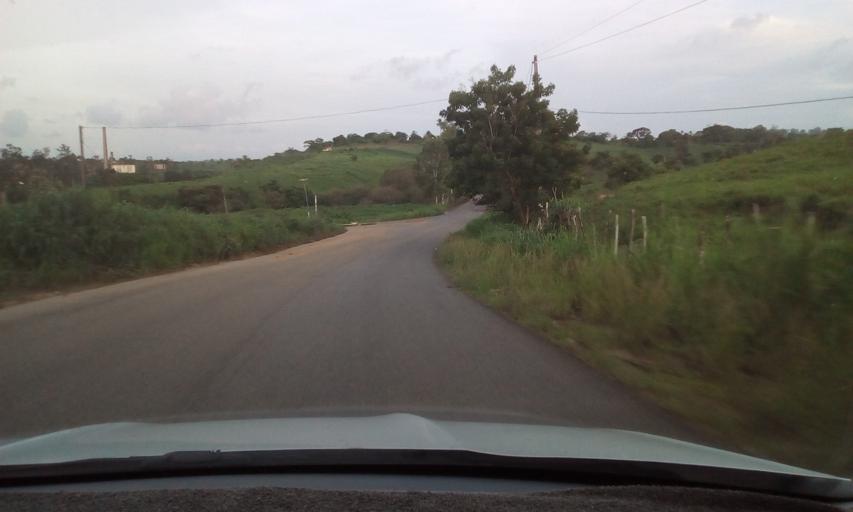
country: BR
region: Pernambuco
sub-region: Condado
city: Condado
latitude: -7.5980
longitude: -35.2167
